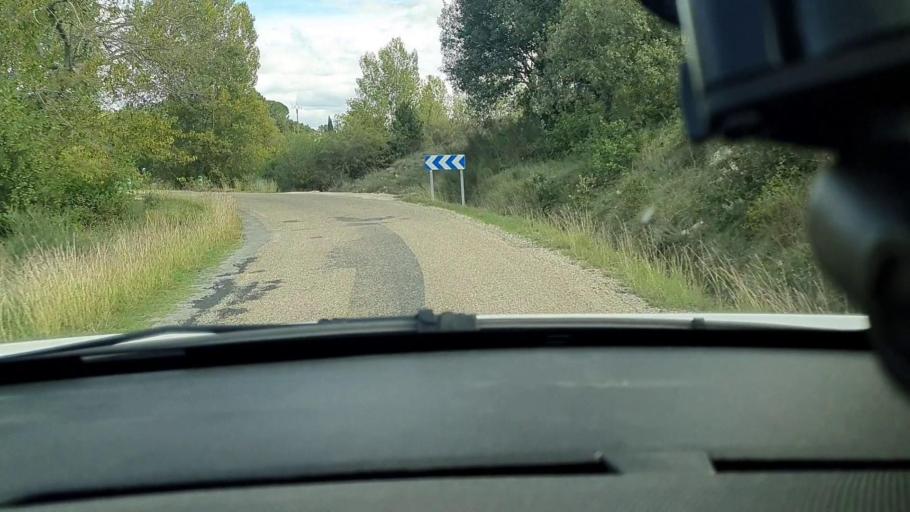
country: FR
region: Languedoc-Roussillon
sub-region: Departement du Gard
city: Salindres
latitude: 44.1684
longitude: 4.2719
